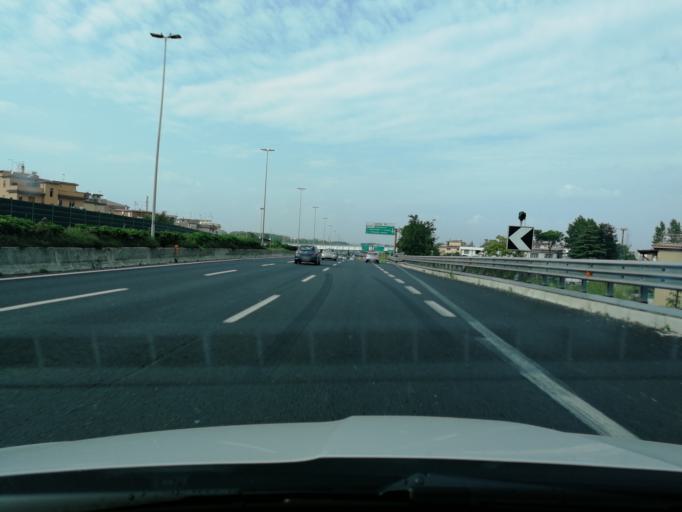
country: IT
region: Latium
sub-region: Citta metropolitana di Roma Capitale
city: Setteville
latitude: 41.9164
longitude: 12.6148
